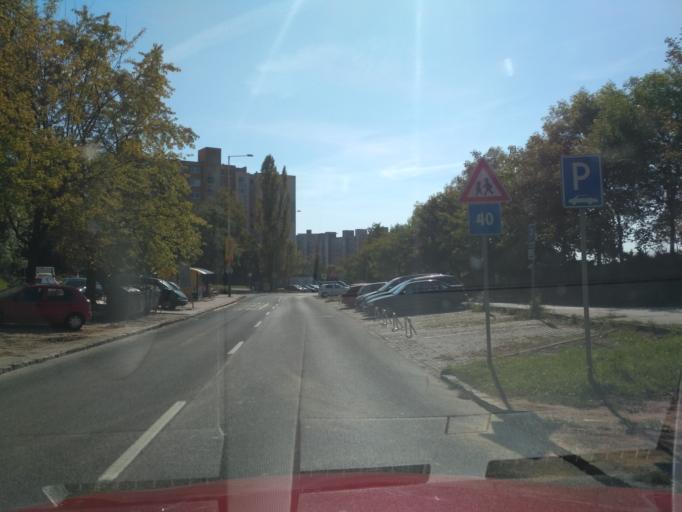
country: SK
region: Kosicky
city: Kosice
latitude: 48.7594
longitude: 21.2685
